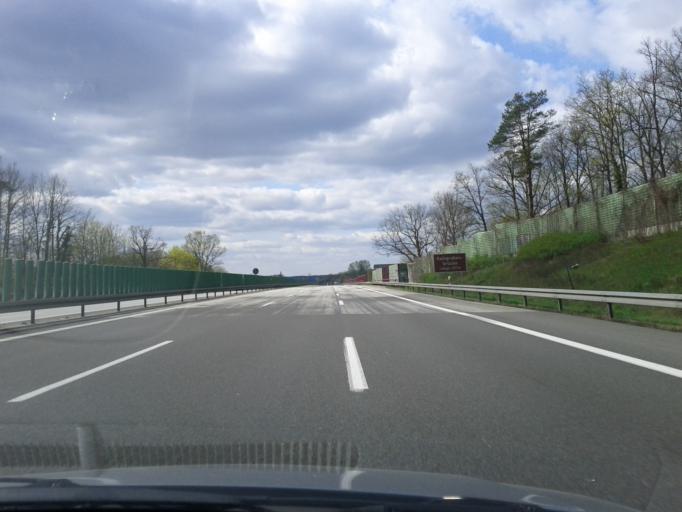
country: DE
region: Brandenburg
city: Woltersdorf
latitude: 52.4658
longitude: 13.7864
